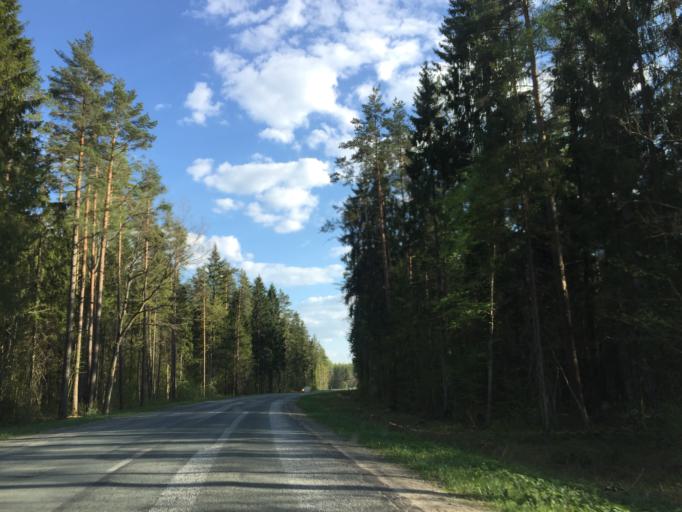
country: LV
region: Sigulda
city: Sigulda
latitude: 57.2216
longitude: 24.8551
